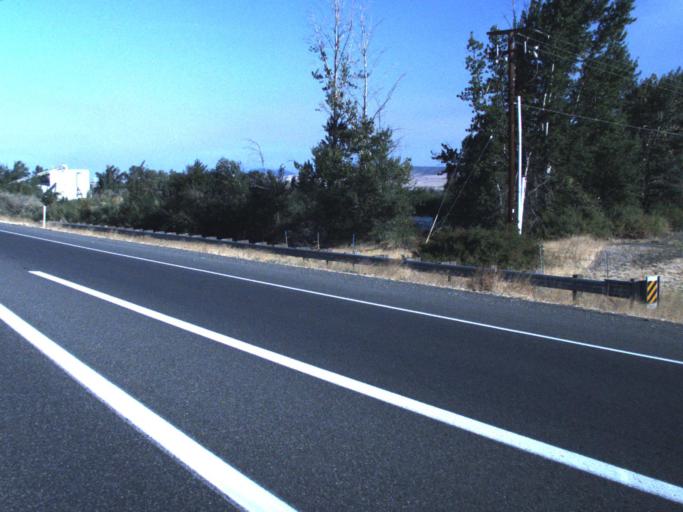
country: US
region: Washington
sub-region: Kittitas County
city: Ellensburg
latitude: 47.0089
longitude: -120.5952
